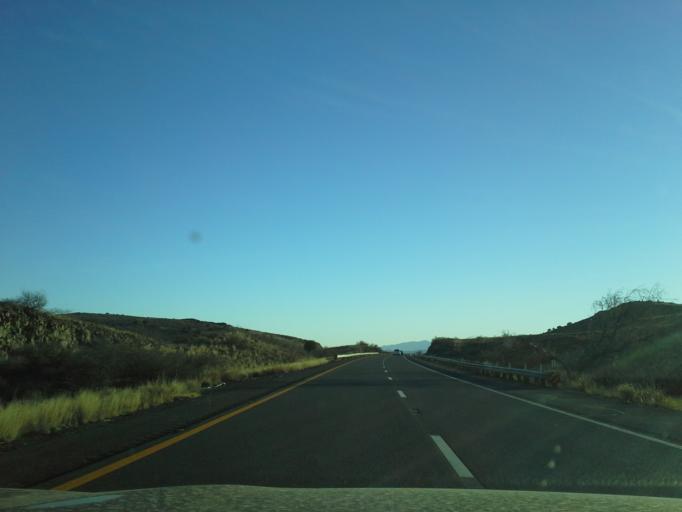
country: US
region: Arizona
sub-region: Yavapai County
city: Cordes Lakes
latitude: 34.4679
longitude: -112.0266
